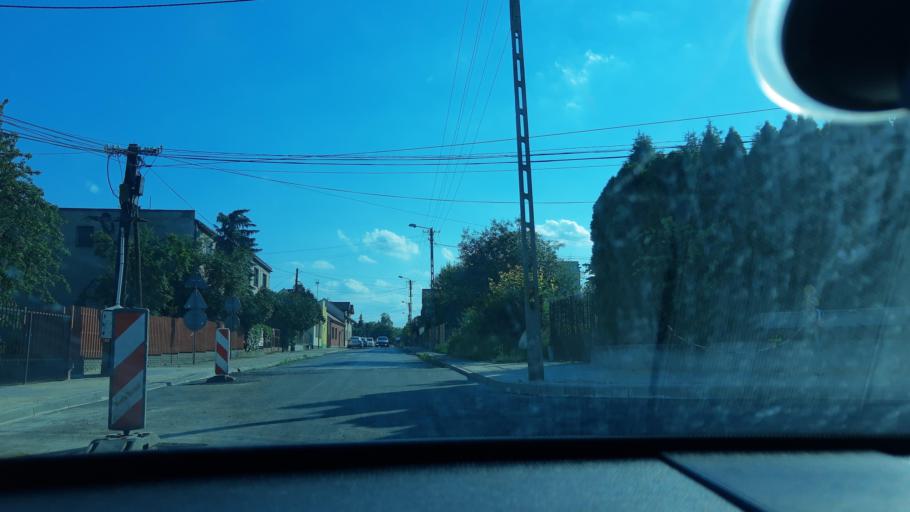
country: PL
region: Lodz Voivodeship
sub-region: Powiat sieradzki
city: Sieradz
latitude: 51.6022
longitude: 18.7327
